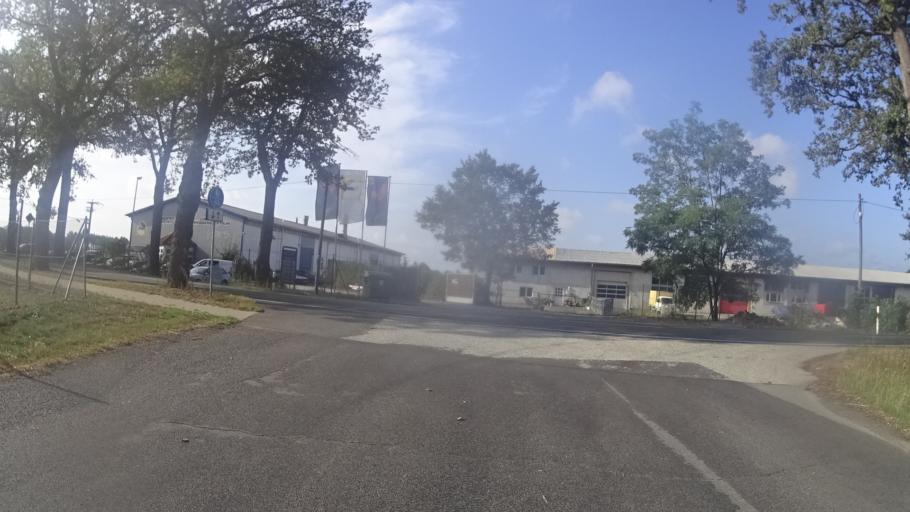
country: DE
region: Brandenburg
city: Cumlosen
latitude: 53.0239
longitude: 11.6796
